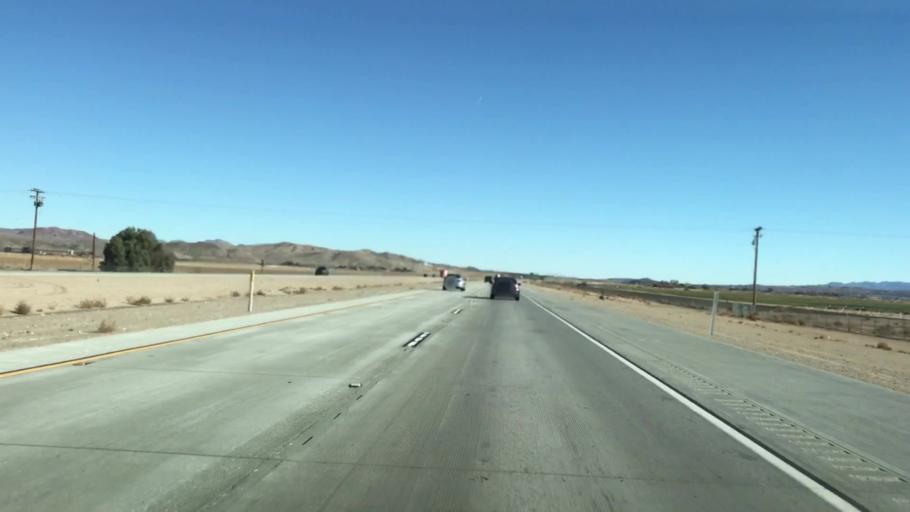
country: US
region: California
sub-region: San Bernardino County
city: Lenwood
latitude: 34.9154
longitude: -117.1376
